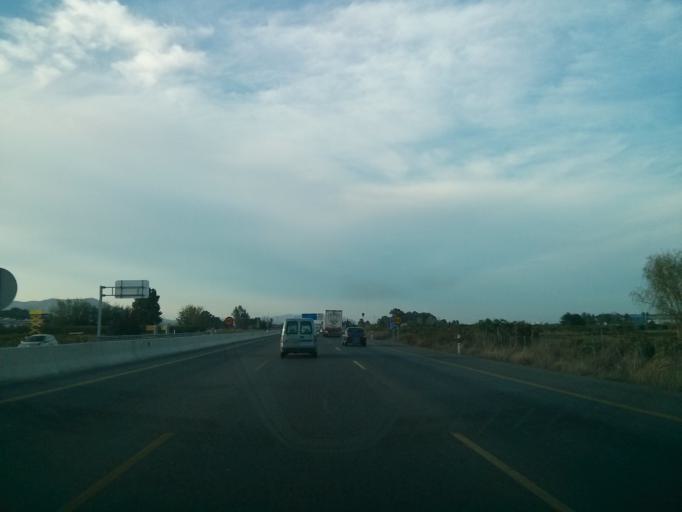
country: ES
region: Valencia
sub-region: Provincia de Valencia
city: Puig
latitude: 39.5797
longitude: -0.2945
